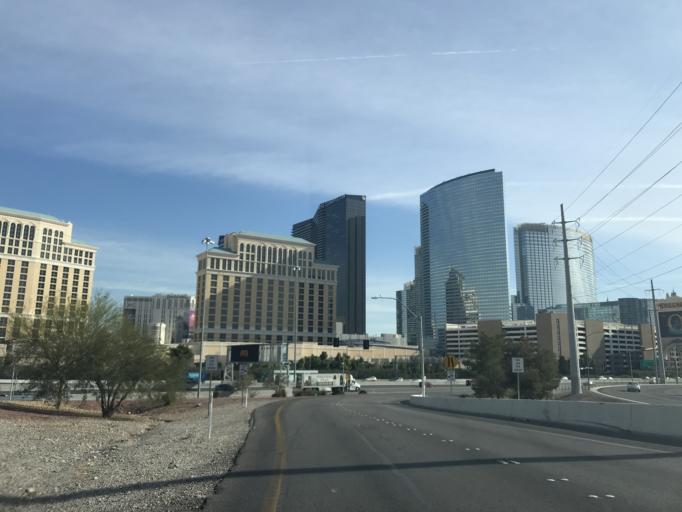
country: US
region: Nevada
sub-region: Clark County
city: Paradise
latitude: 36.1128
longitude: -115.1821
